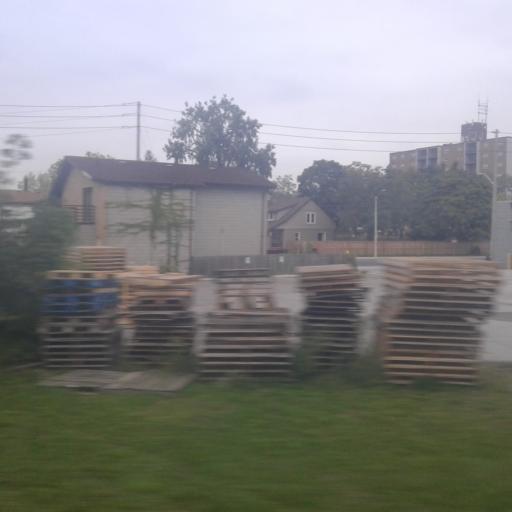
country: CA
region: Ontario
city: Windsor
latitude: 42.3240
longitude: -82.9977
